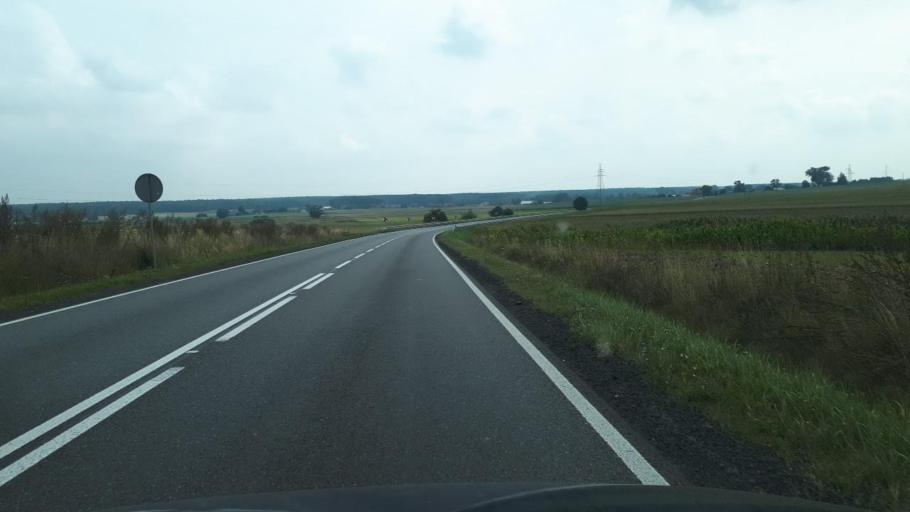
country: PL
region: Greater Poland Voivodeship
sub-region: Powiat ostrzeszowski
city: Ostrzeszow
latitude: 51.3676
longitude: 17.9443
